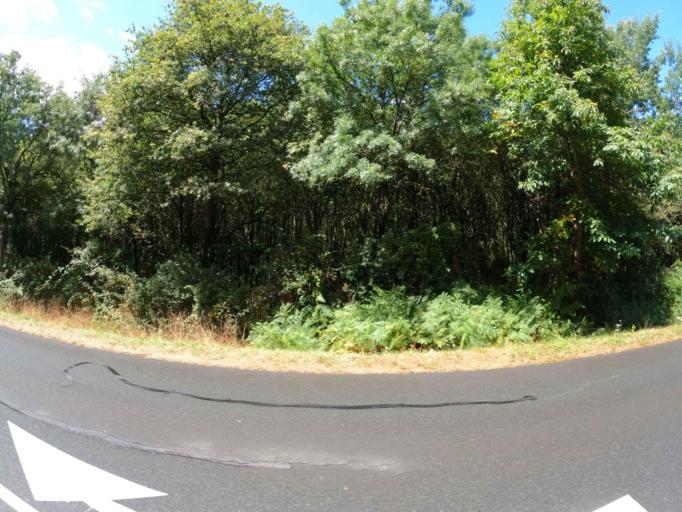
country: FR
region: Pays de la Loire
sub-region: Departement de Maine-et-Loire
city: Feneu
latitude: 47.6142
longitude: -0.5847
